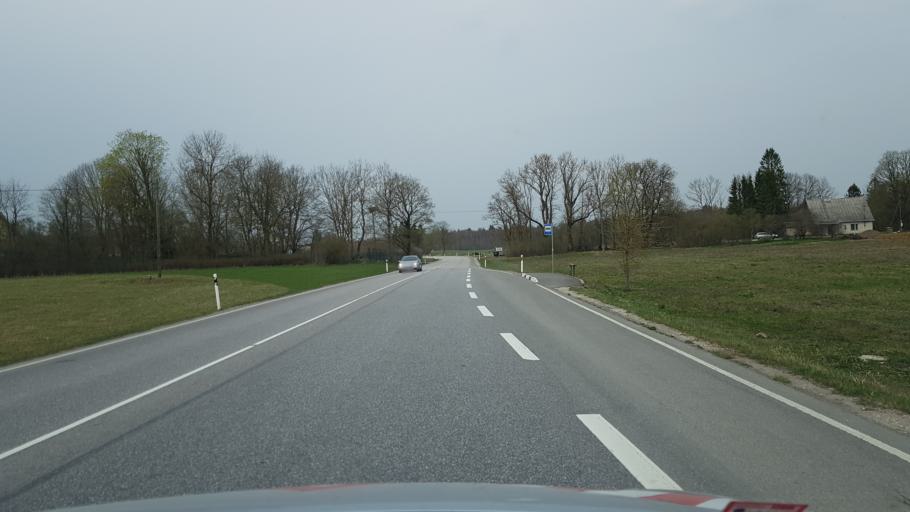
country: EE
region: Harju
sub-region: Raasiku vald
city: Arukula
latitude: 59.3693
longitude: 25.0271
